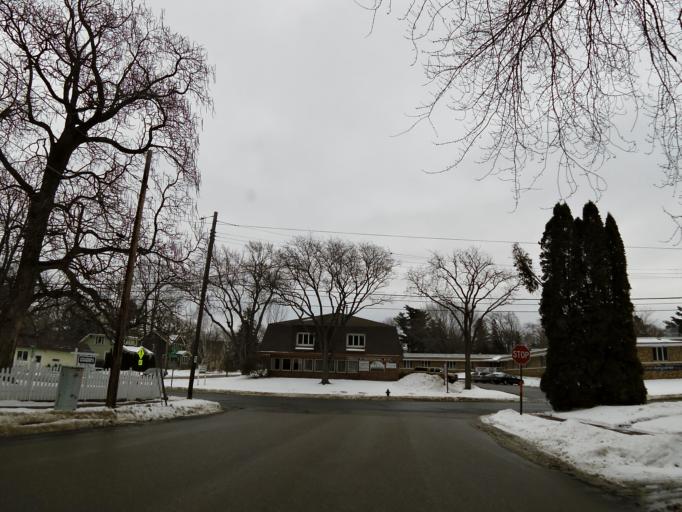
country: US
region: Minnesota
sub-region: Washington County
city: Stillwater
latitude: 45.0530
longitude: -92.8196
